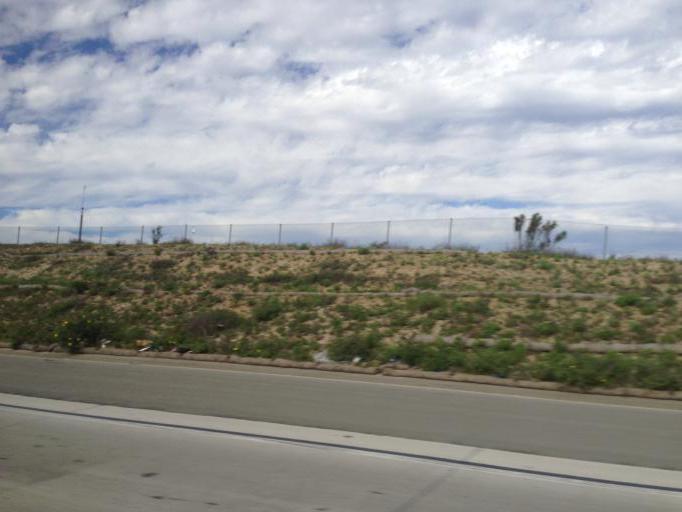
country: MX
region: Baja California
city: Tijuana
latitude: 32.5666
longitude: -117.0055
